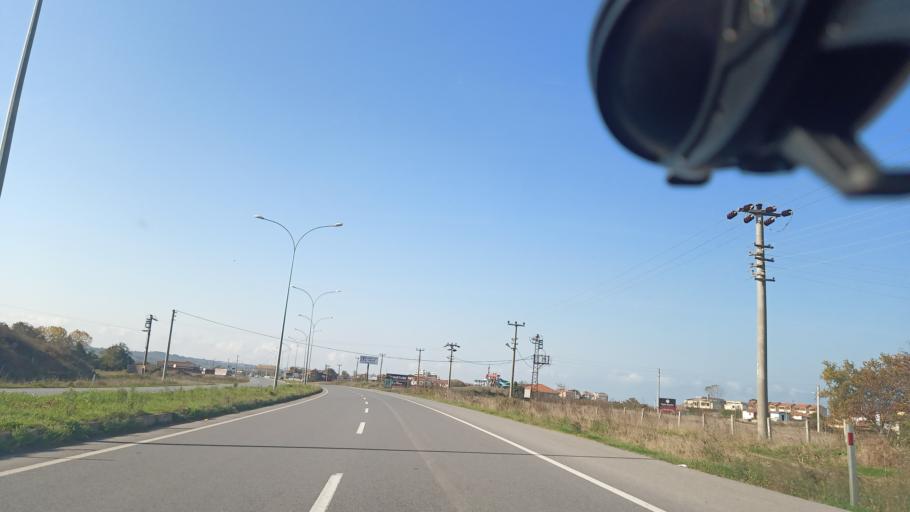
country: TR
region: Sakarya
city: Karasu
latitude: 41.0869
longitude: 30.7498
